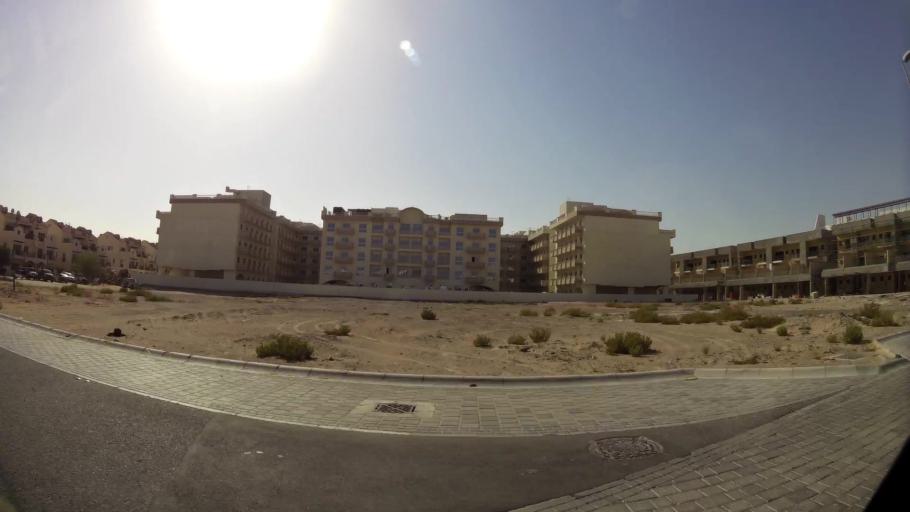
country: AE
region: Dubai
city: Dubai
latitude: 25.0676
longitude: 55.2059
